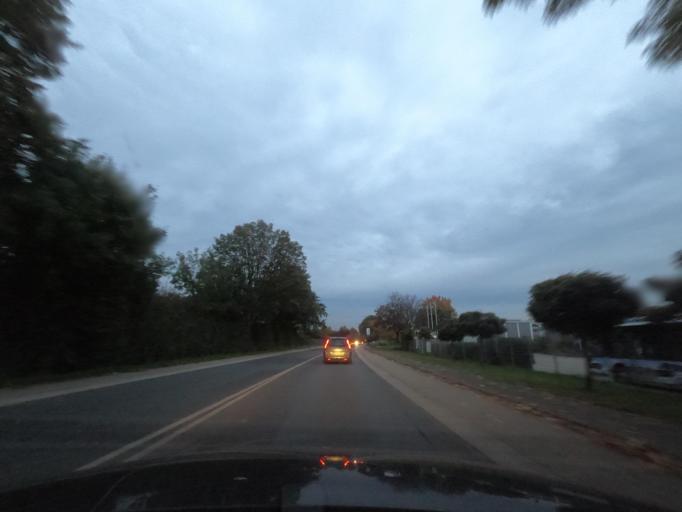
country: DE
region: North Rhine-Westphalia
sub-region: Regierungsbezirk Dusseldorf
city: Wesel
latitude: 51.6745
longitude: 6.6310
